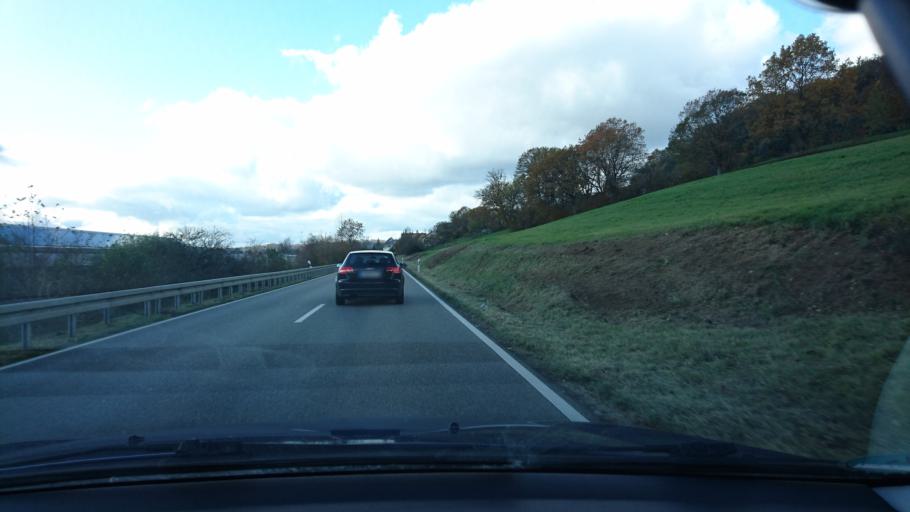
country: DE
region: Baden-Wuerttemberg
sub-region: Regierungsbezirk Stuttgart
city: Abtsgmund
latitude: 48.8953
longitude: 10.0282
